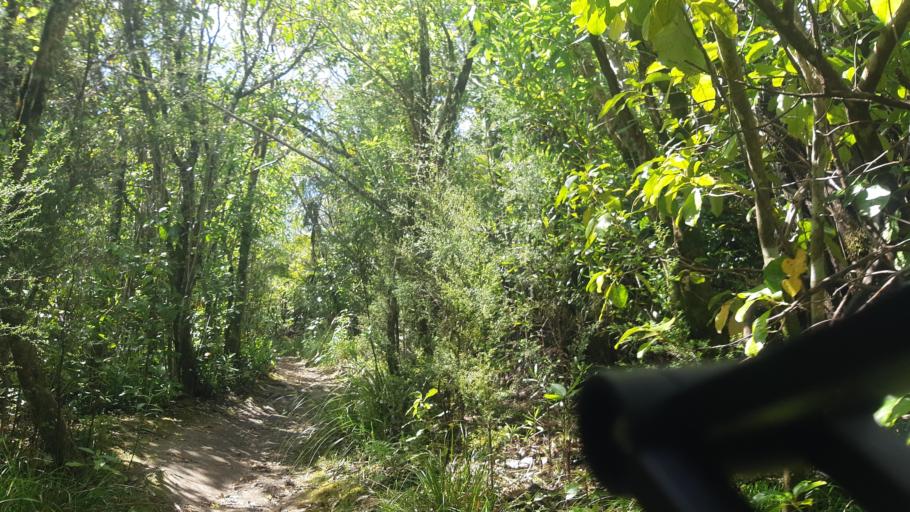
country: NZ
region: Marlborough
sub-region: Marlborough District
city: Picton
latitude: -41.2572
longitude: 174.0381
